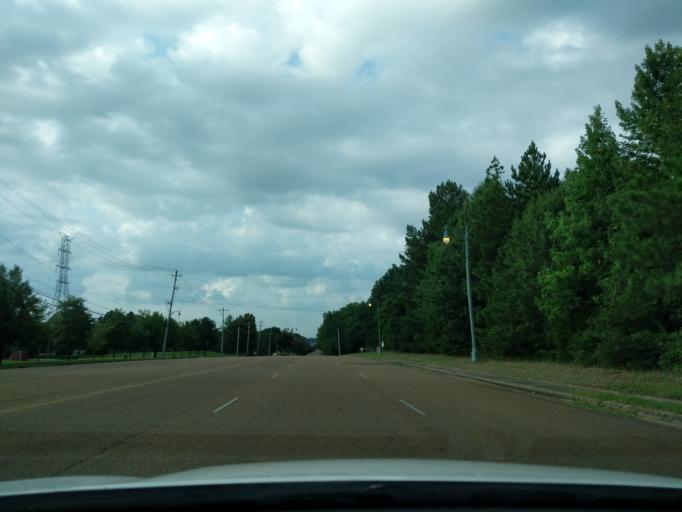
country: US
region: Tennessee
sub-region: Shelby County
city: Germantown
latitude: 35.0418
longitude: -89.7599
